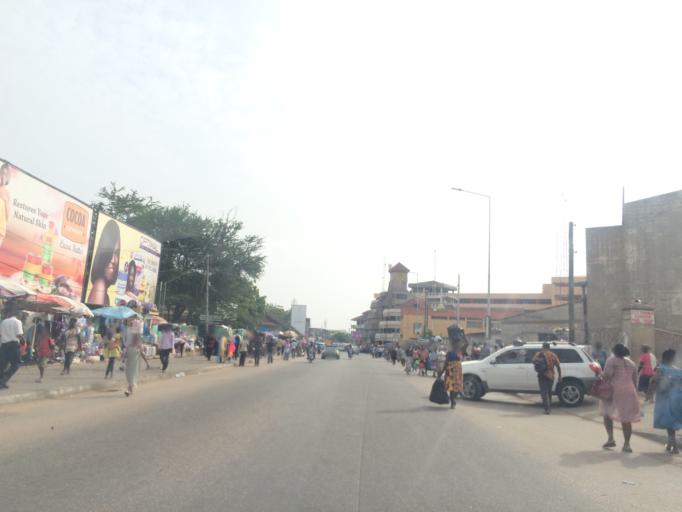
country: GH
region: Greater Accra
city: Accra
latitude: 5.5478
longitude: -0.2048
